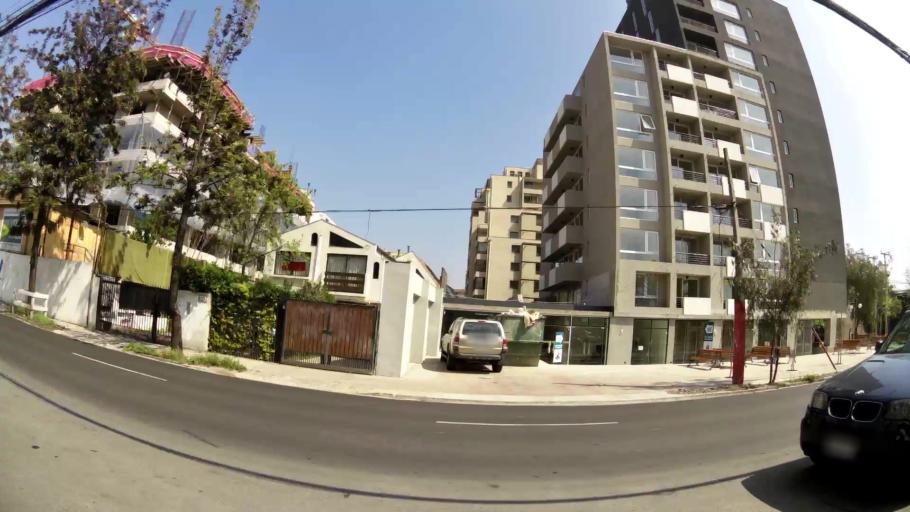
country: CL
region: Santiago Metropolitan
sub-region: Provincia de Santiago
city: Villa Presidente Frei, Nunoa, Santiago, Chile
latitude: -33.4466
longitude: -70.5990
